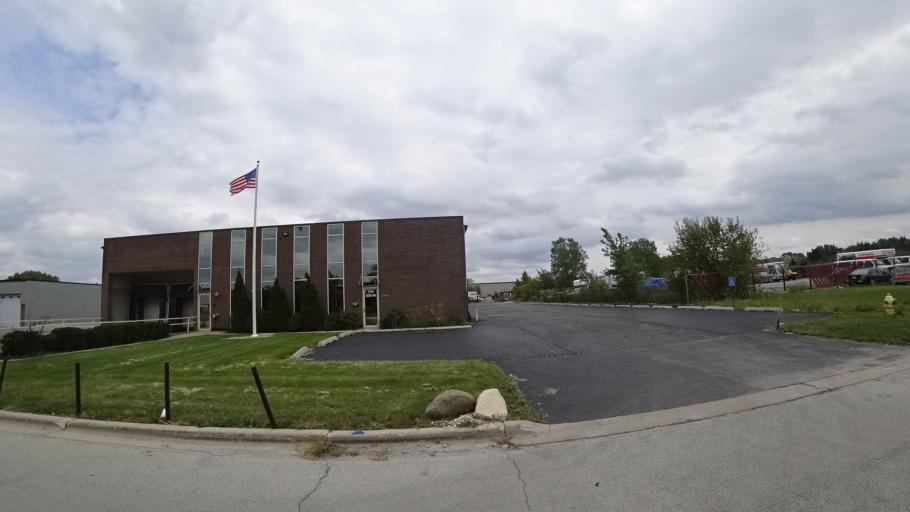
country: US
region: Illinois
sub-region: Cook County
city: Tinley Park
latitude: 41.5717
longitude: -87.8016
